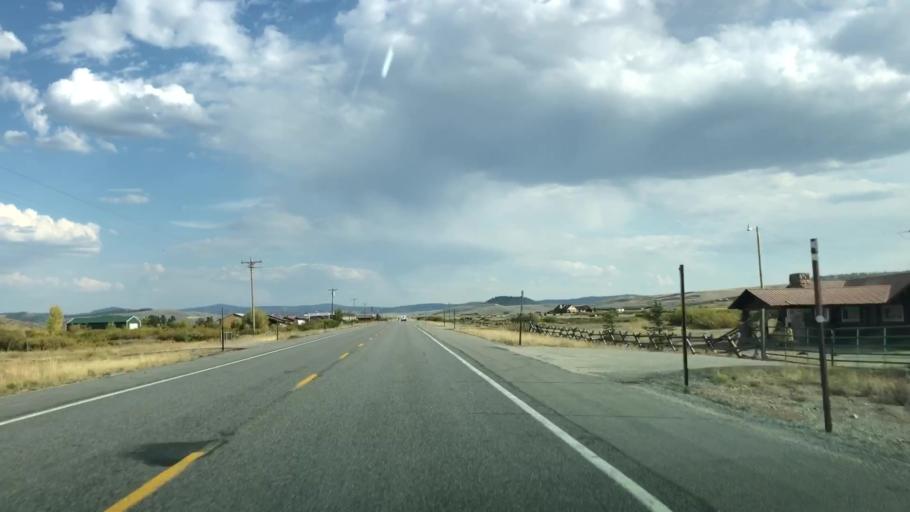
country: US
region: Wyoming
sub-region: Teton County
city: Hoback
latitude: 43.2063
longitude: -110.4119
